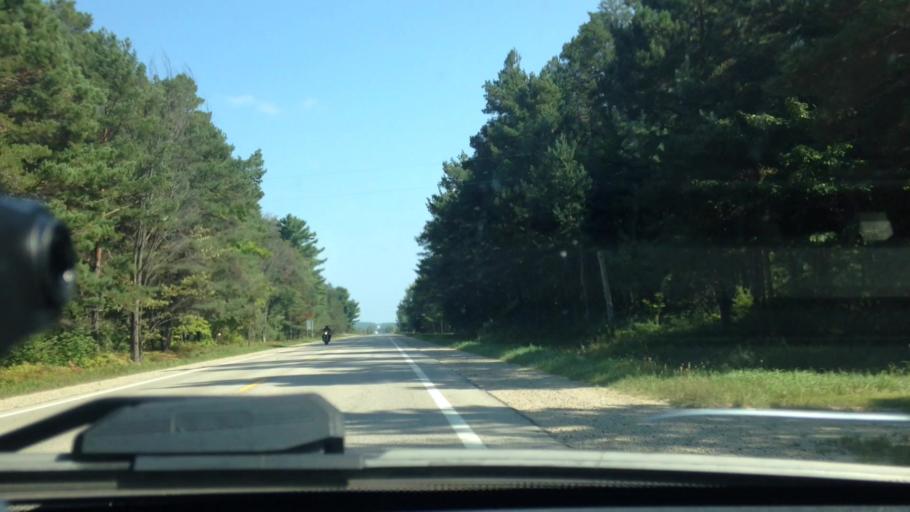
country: US
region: Michigan
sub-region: Luce County
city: Newberry
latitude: 46.3102
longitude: -85.6379
